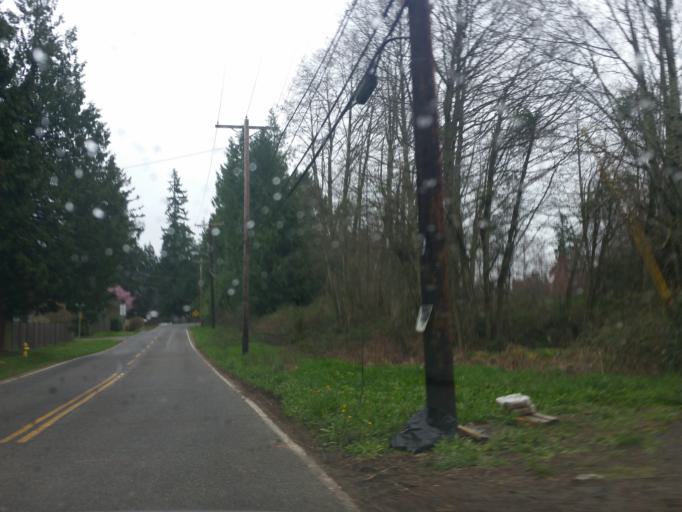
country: US
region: Washington
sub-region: Snohomish County
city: Meadowdale
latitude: 47.8489
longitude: -122.3249
